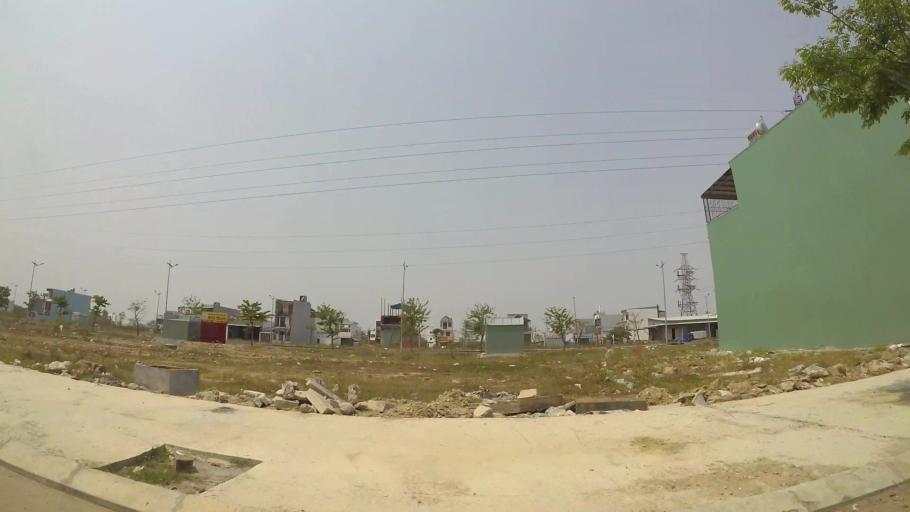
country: VN
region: Da Nang
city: Ngu Hanh Son
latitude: 16.0165
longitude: 108.2293
